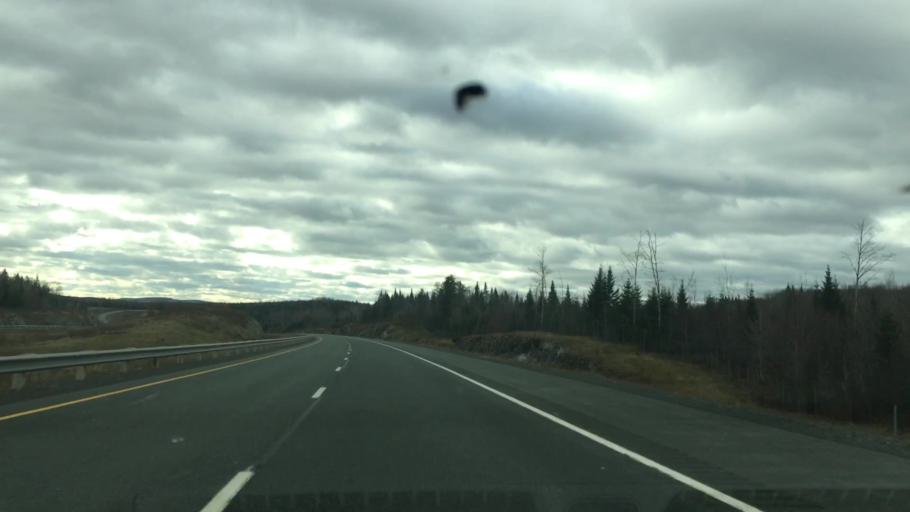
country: US
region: Maine
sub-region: Aroostook County
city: Easton
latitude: 46.6055
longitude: -67.7441
